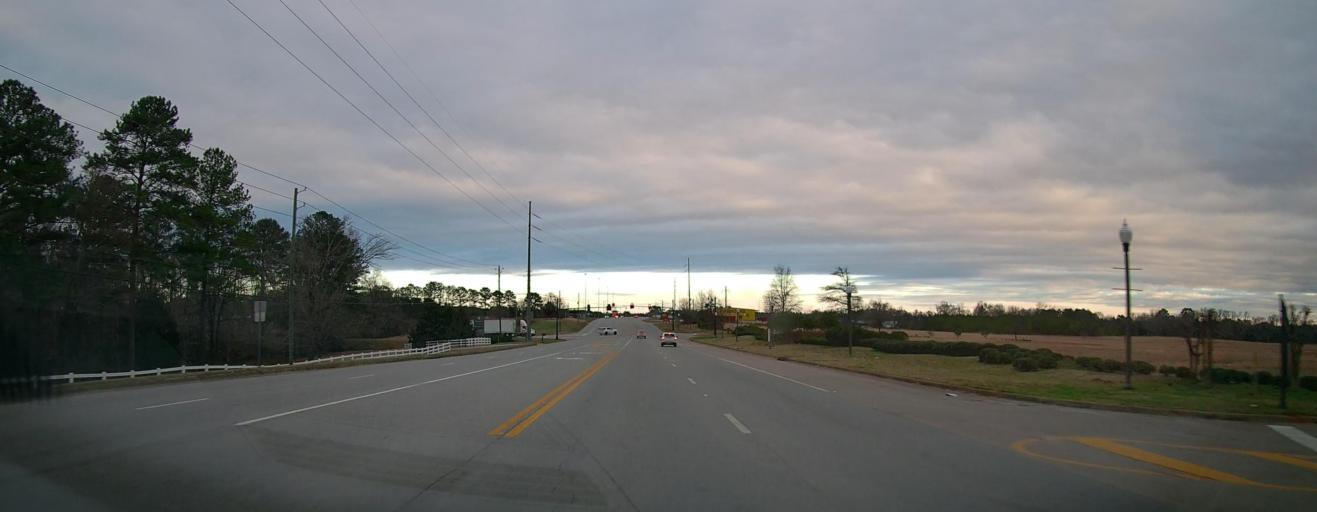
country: US
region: Alabama
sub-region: Chambers County
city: Huguley
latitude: 32.8261
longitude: -85.2176
